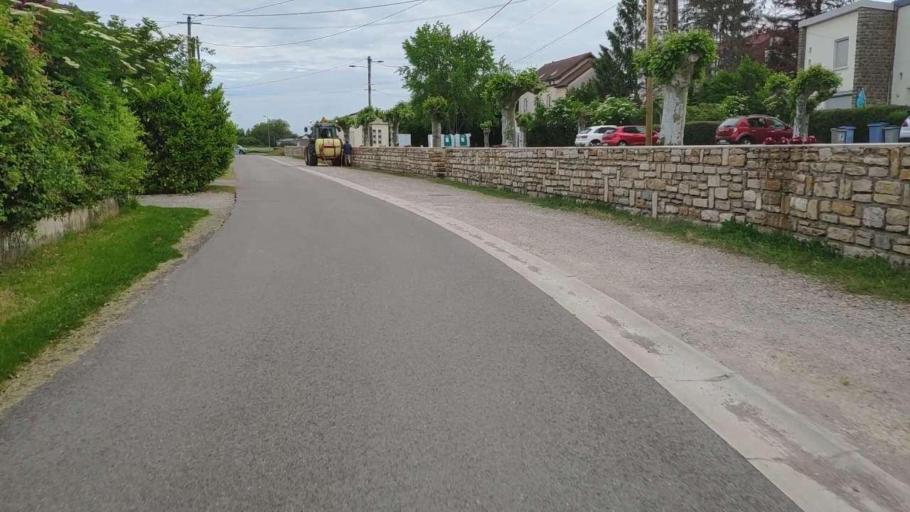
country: FR
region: Franche-Comte
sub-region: Departement du Jura
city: Bletterans
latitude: 46.7481
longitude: 5.4616
